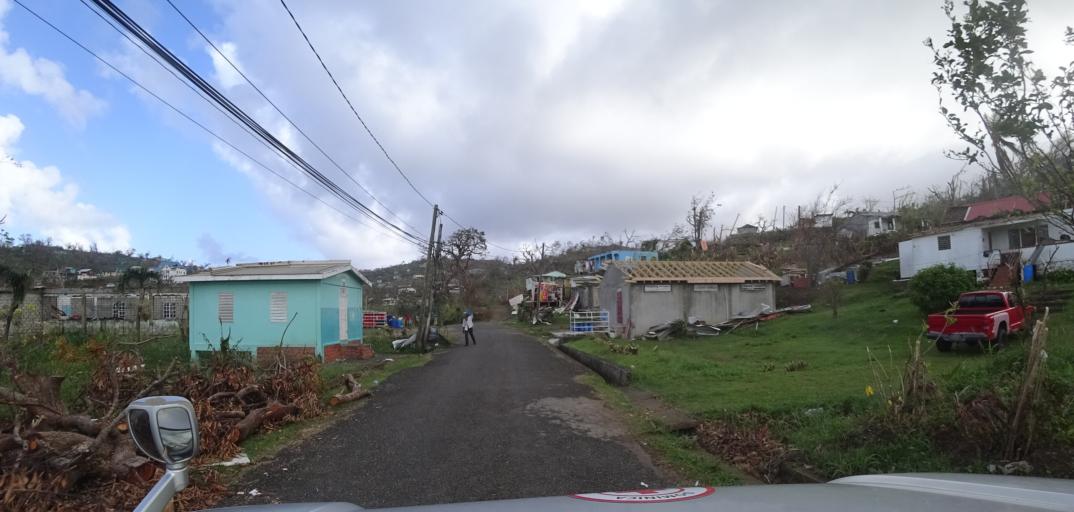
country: DM
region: Saint Andrew
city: Marigot
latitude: 15.5386
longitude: -61.2865
